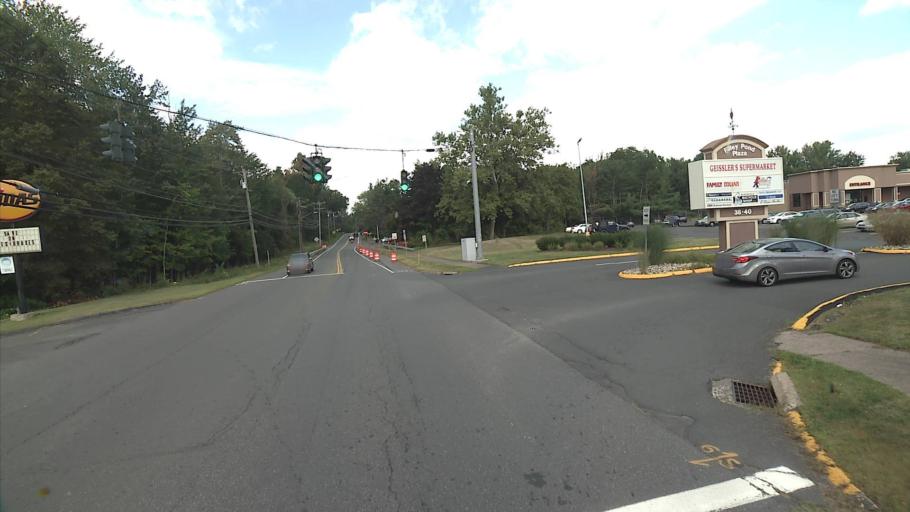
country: US
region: Connecticut
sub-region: Hartford County
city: Blue Hills
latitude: 41.8358
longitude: -72.7382
